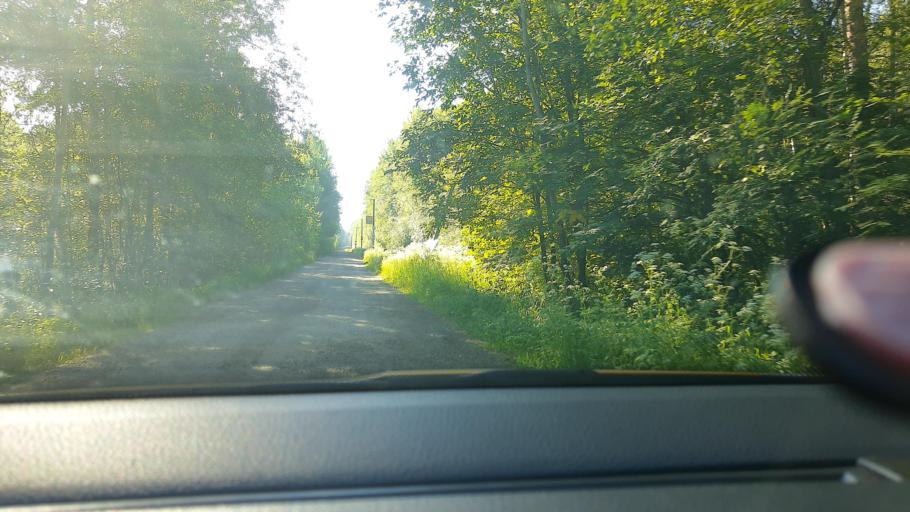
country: RU
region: Moskovskaya
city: Elektrogorsk
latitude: 55.8998
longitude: 38.7034
